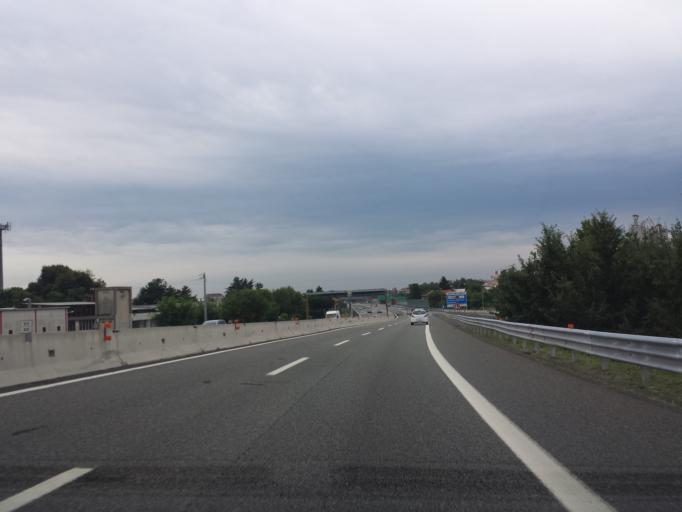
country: IT
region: Lombardy
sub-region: Provincia di Varese
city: Gallarate
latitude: 45.6736
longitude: 8.8010
